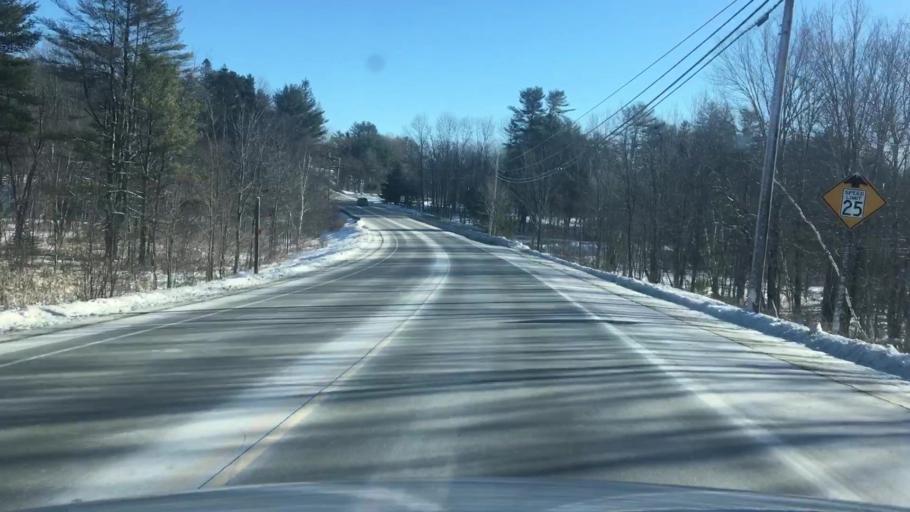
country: US
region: Maine
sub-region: Kennebec County
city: Readfield
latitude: 44.3879
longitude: -69.9740
